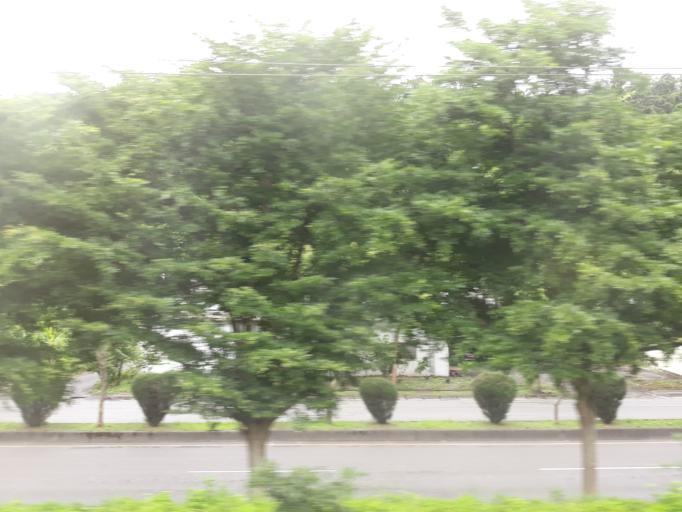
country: TW
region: Taiwan
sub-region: Yilan
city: Yilan
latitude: 24.6152
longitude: 121.8170
